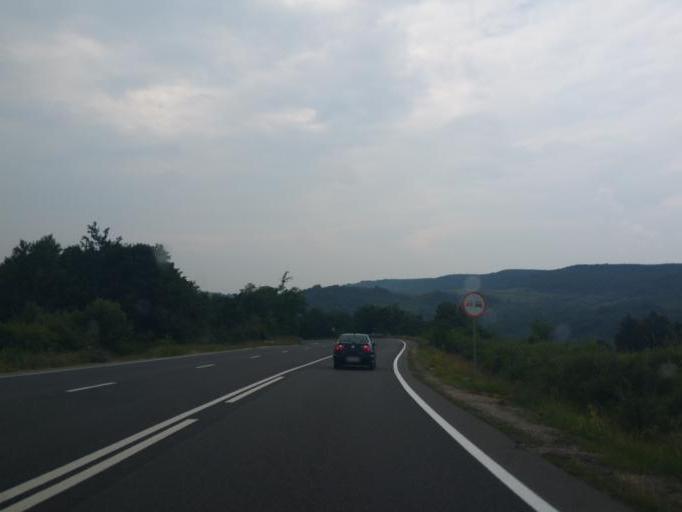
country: RO
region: Cluj
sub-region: Comuna Sanpaul
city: Sanpaul
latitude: 46.9460
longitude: 23.3780
